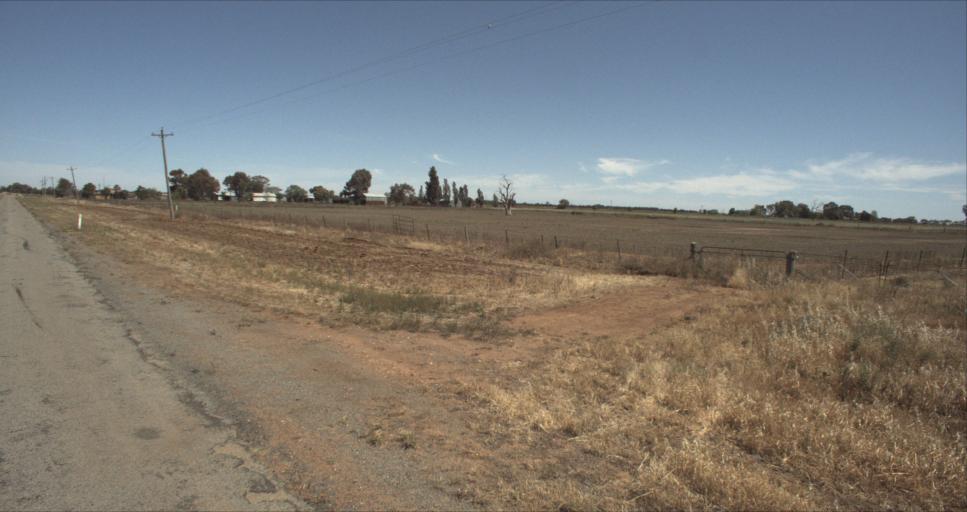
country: AU
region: New South Wales
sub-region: Leeton
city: Leeton
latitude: -34.5079
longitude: 146.3446
